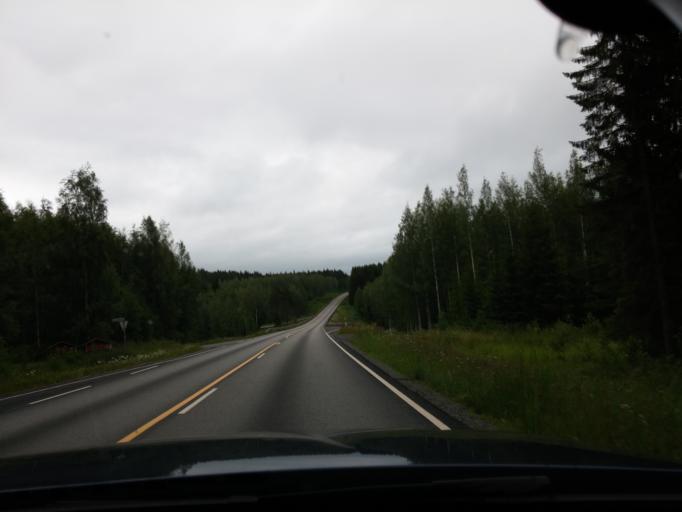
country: FI
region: Central Finland
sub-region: Saarijaervi-Viitasaari
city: Saarijaervi
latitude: 62.6829
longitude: 25.2405
